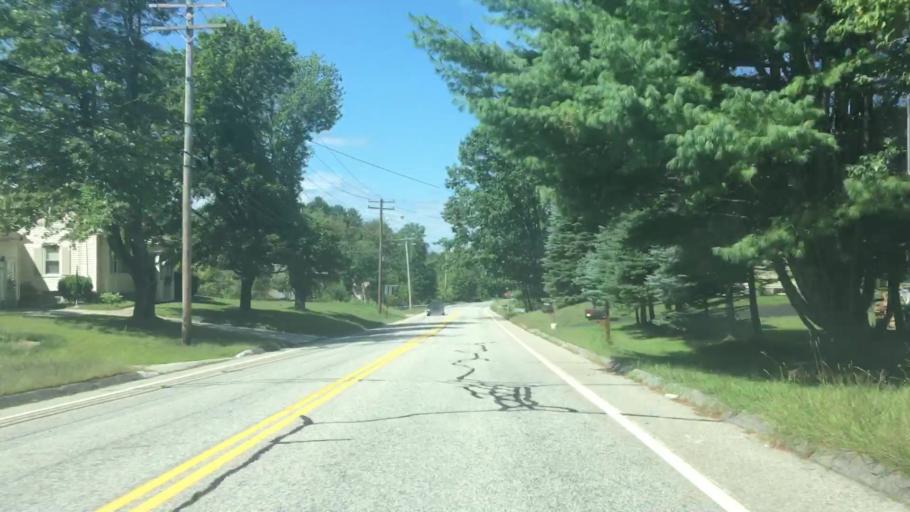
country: US
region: Maine
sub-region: Androscoggin County
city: Sabattus
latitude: 44.0894
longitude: -70.1452
